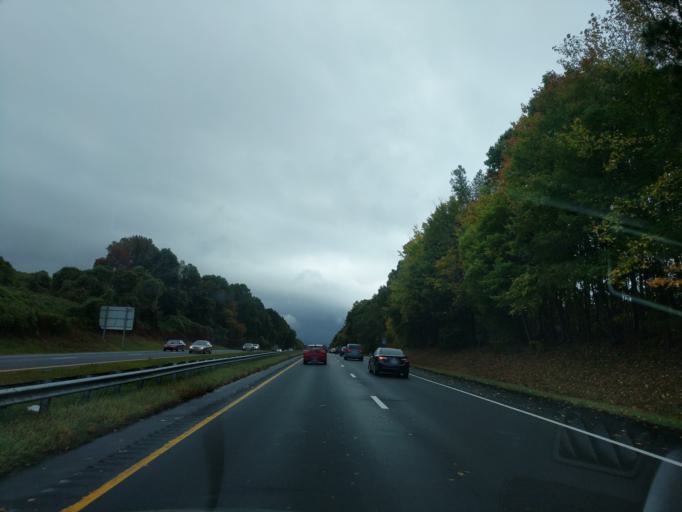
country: US
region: North Carolina
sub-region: Orange County
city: Hillsborough
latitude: 36.0573
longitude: -79.0772
